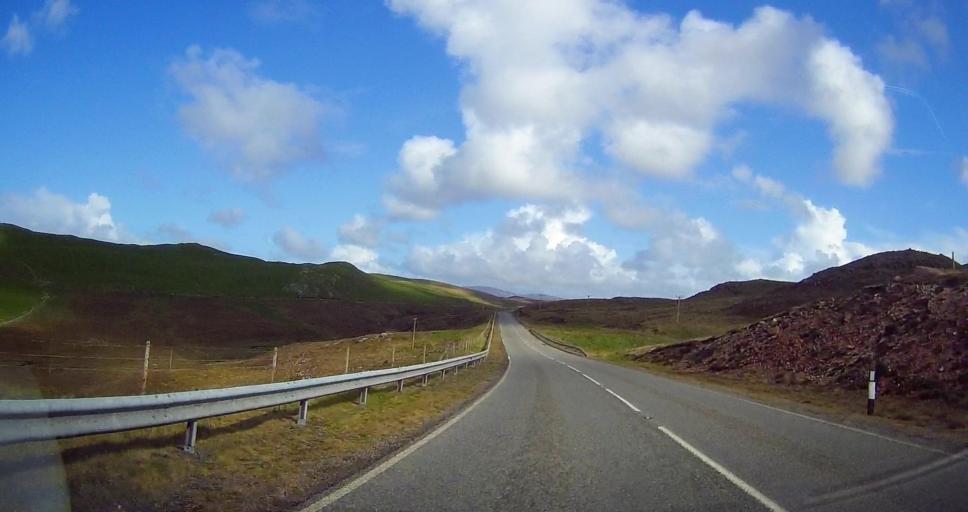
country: GB
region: Scotland
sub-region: Shetland Islands
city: Lerwick
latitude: 60.4195
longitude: -1.3938
